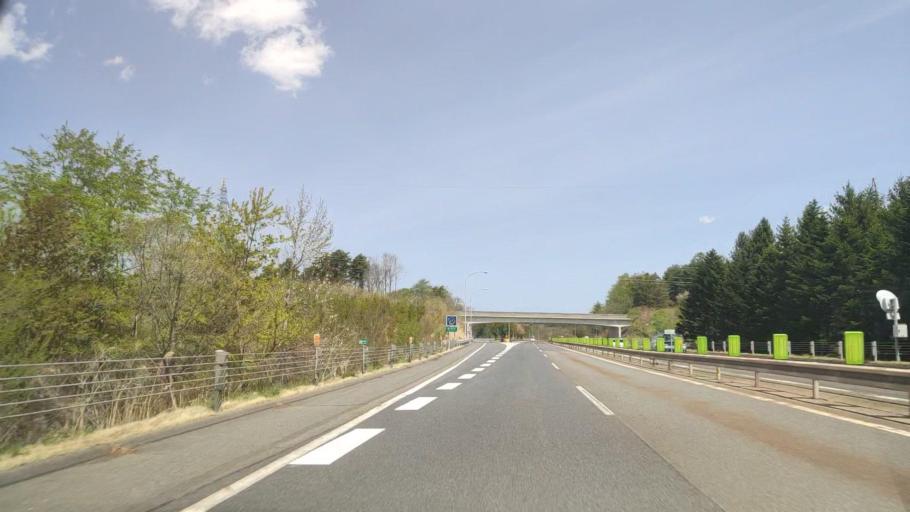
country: JP
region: Aomori
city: Hachinohe
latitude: 40.4408
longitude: 141.4484
